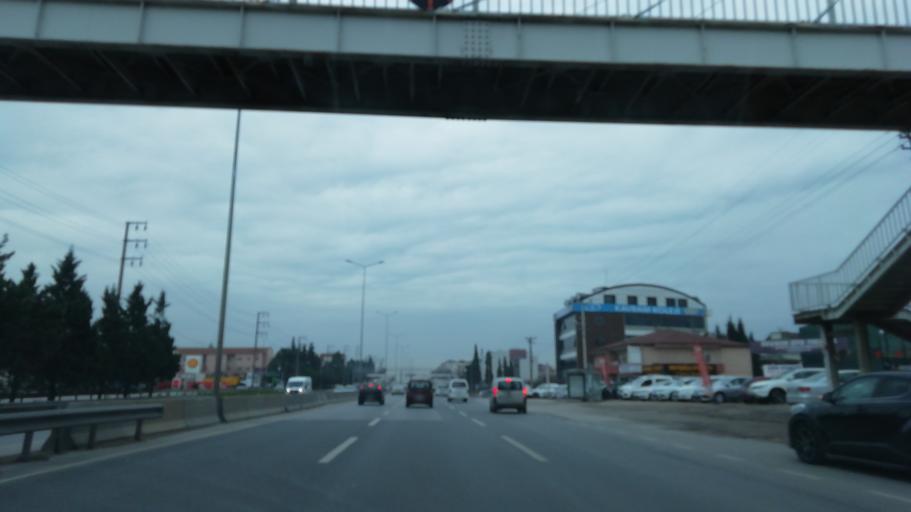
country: TR
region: Kocaeli
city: Derince
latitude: 40.7573
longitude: 29.8039
